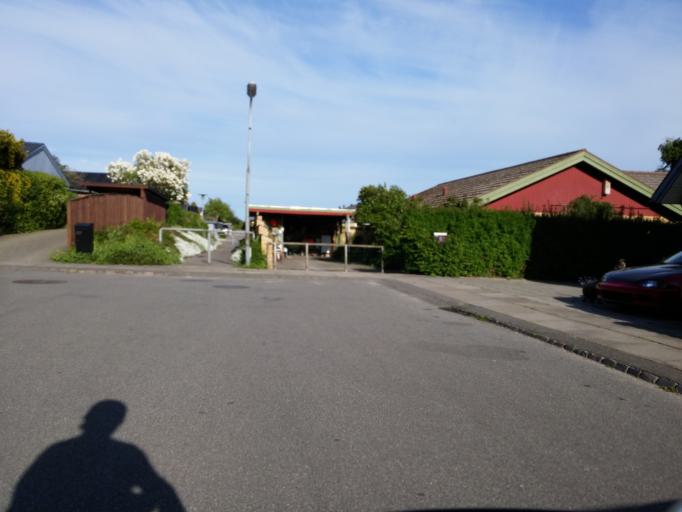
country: DK
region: South Denmark
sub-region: Odense Kommune
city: Seden
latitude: 55.4011
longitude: 10.4448
